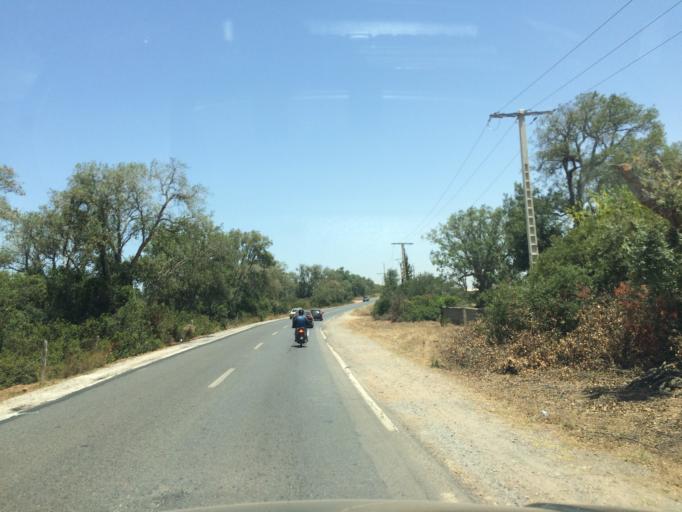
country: MA
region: Rabat-Sale-Zemmour-Zaer
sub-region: Skhirate-Temara
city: Temara
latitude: 33.9019
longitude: -6.8261
